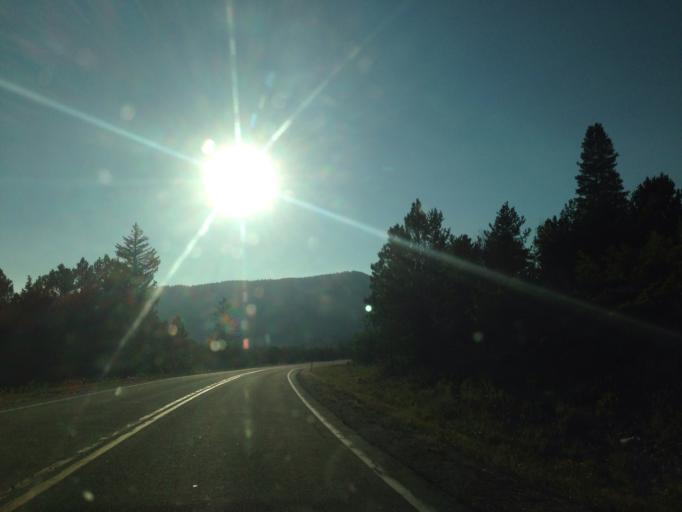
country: US
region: Utah
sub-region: Summit County
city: Francis
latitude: 40.5943
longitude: -111.0876
